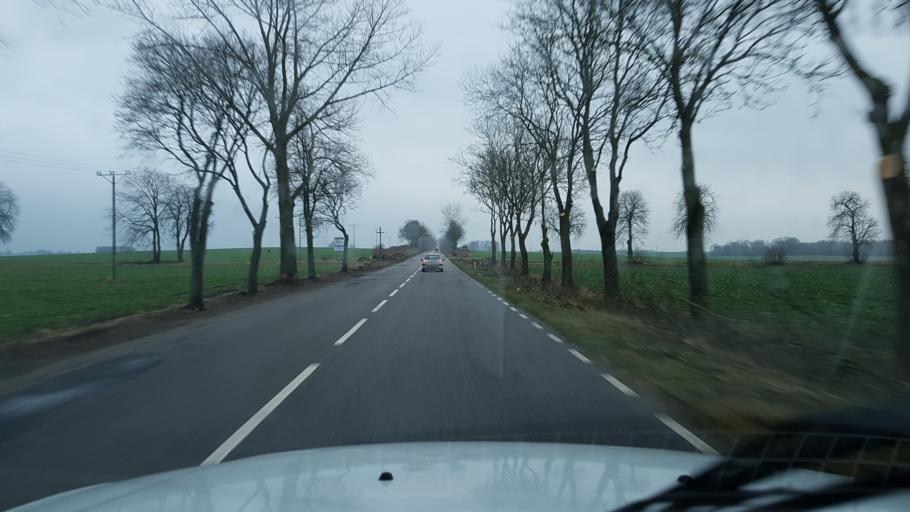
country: PL
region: West Pomeranian Voivodeship
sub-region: Powiat gryficki
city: Ploty
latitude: 53.8424
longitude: 15.2355
